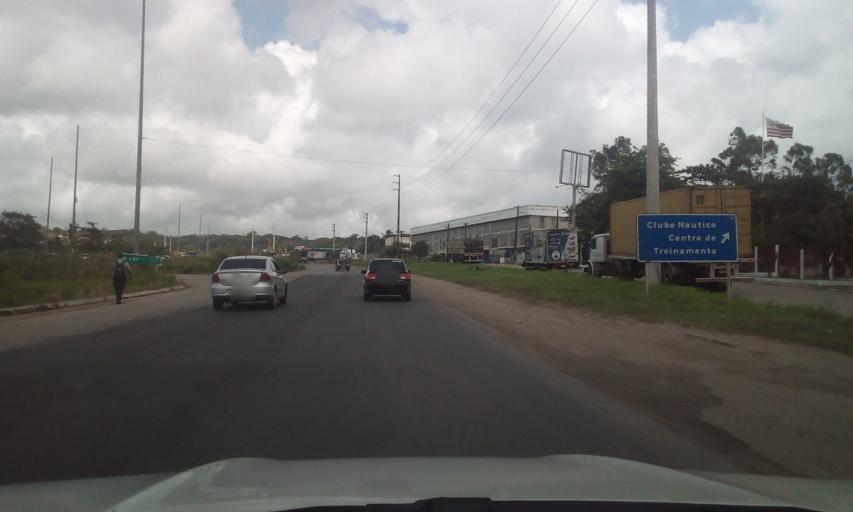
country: BR
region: Pernambuco
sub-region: Paulista
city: Paulista
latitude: -7.9884
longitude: -34.9346
